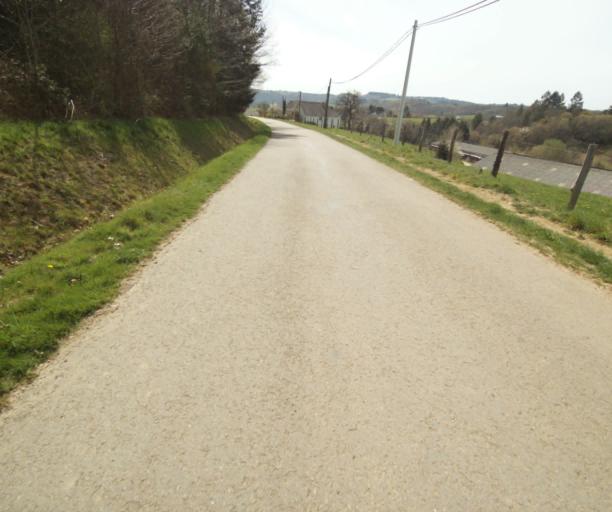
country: FR
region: Limousin
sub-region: Departement de la Correze
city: Naves
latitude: 45.3641
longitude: 1.8016
